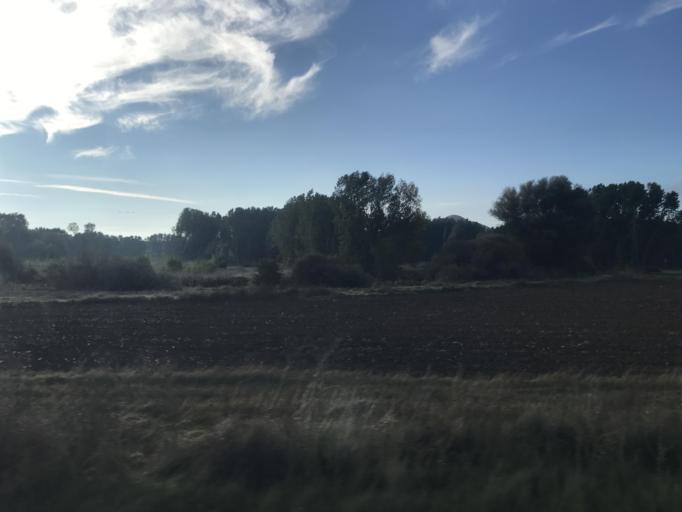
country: ES
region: Castille and Leon
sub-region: Provincia de Burgos
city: Estepar
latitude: 42.2673
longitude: -3.9064
